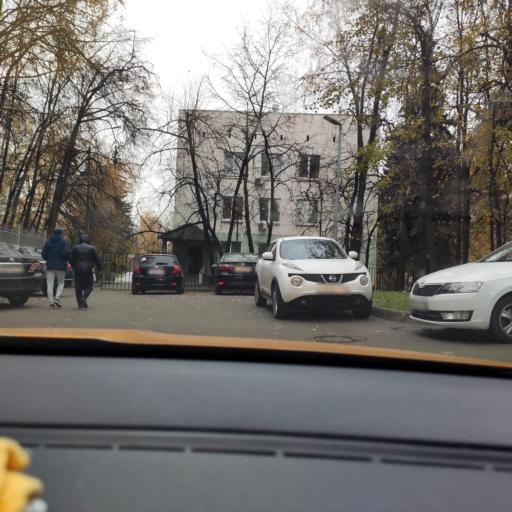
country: RU
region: Moscow
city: Matveyevskoye
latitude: 55.7131
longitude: 37.4784
